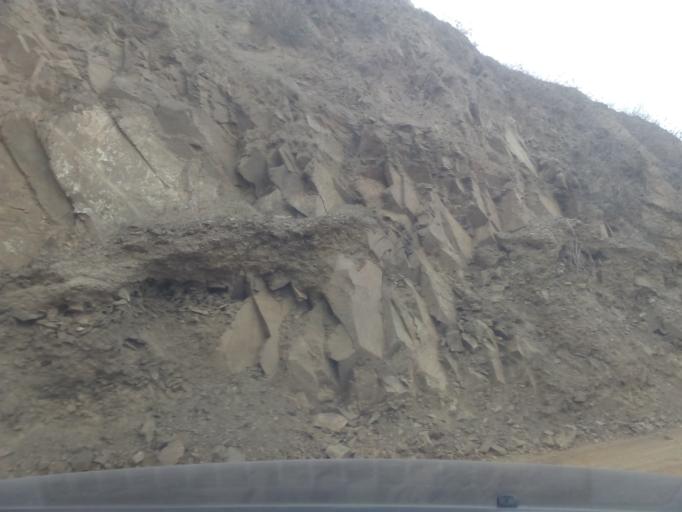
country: PE
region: La Libertad
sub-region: Viru
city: Viru
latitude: -8.3622
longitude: -78.6438
